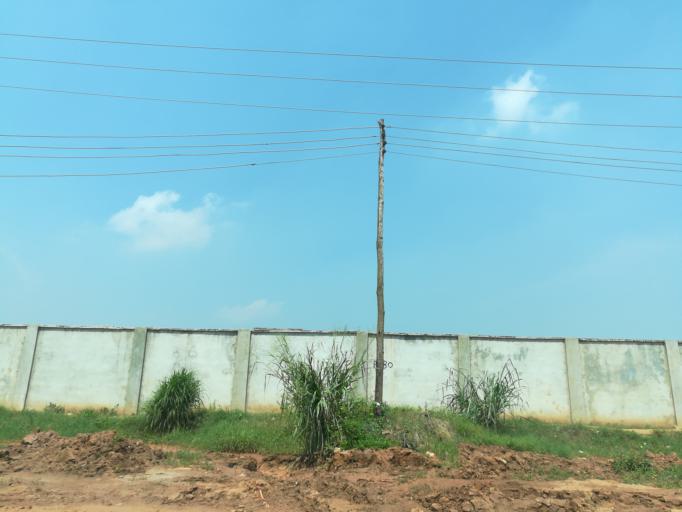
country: NG
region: Lagos
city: Ikorodu
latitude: 6.6548
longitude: 3.4764
